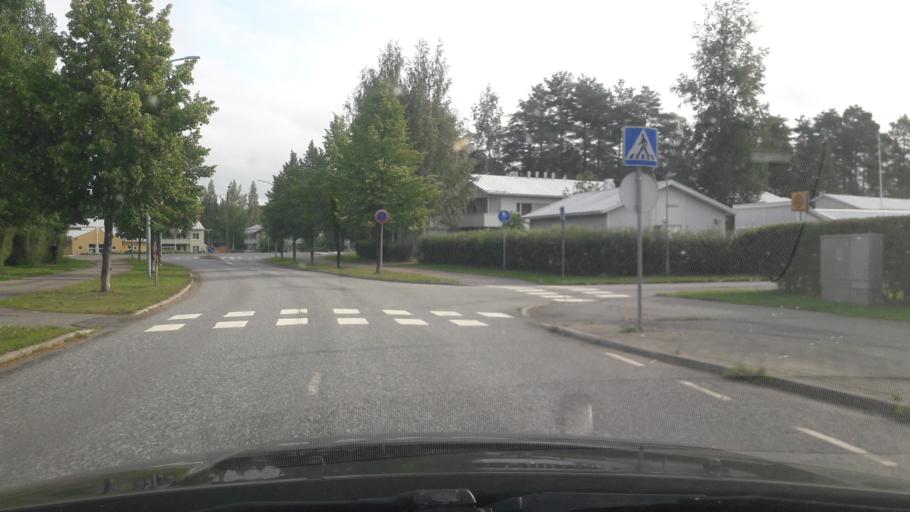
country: FI
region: North Karelia
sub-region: Joensuu
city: Joensuu
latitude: 62.5991
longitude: 29.8276
